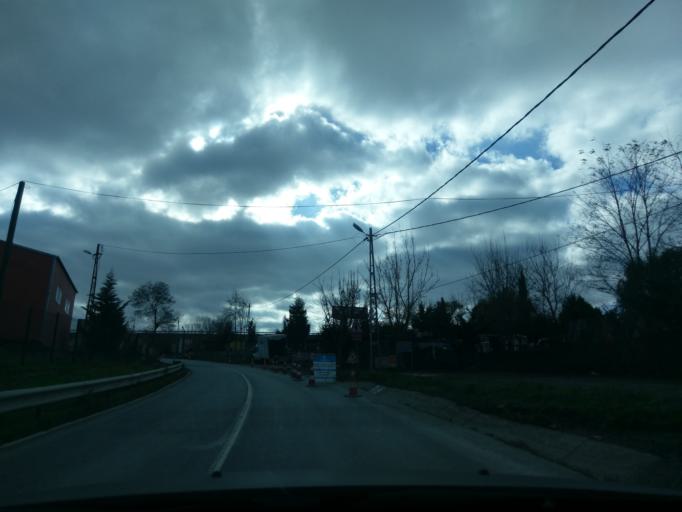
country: TR
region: Istanbul
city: Durusu
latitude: 41.2761
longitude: 28.6610
